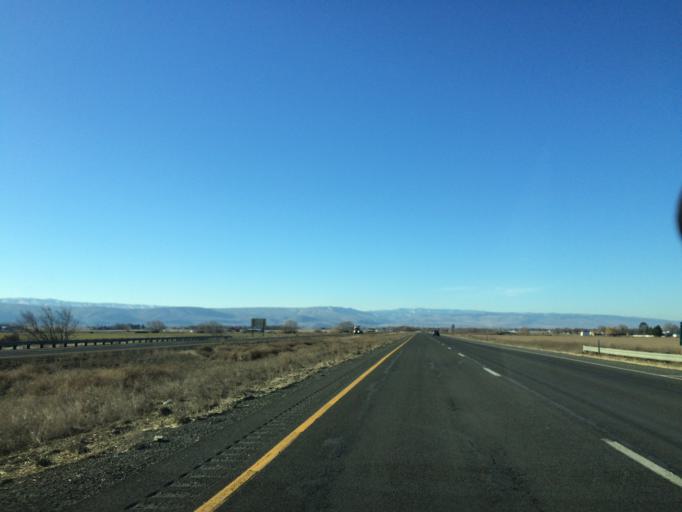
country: US
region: Washington
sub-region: Kittitas County
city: Kittitas
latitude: 46.9717
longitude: -120.4223
